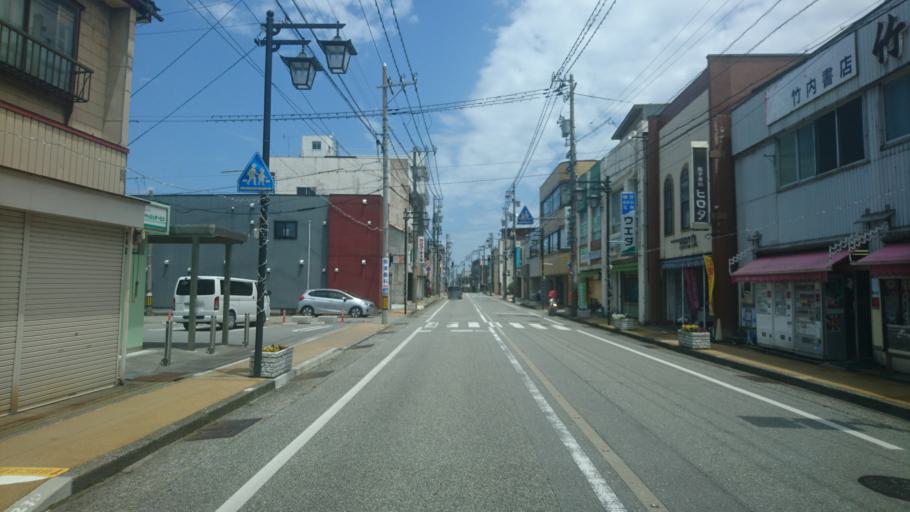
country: JP
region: Toyama
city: Nyuzen
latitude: 36.9390
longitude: 137.5003
